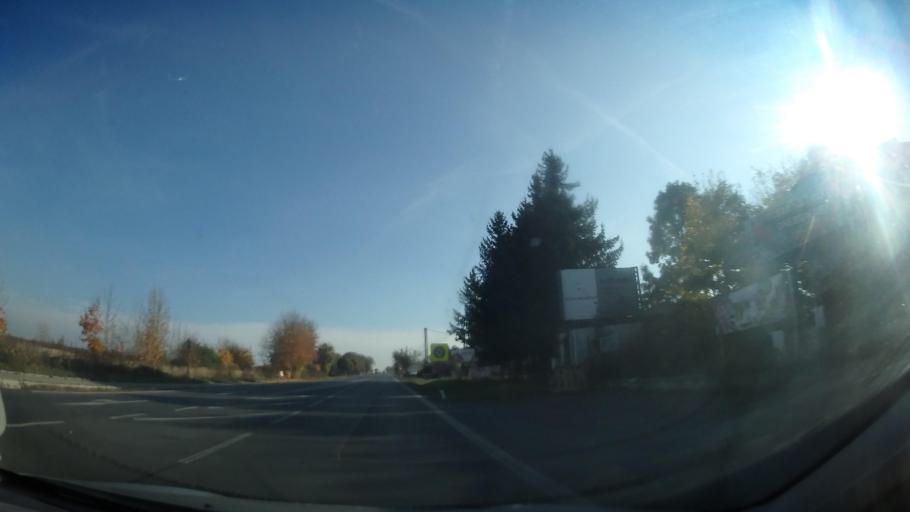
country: CZ
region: Central Bohemia
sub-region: Okres Praha-Vychod
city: Ricany
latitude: 50.0304
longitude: 14.6112
